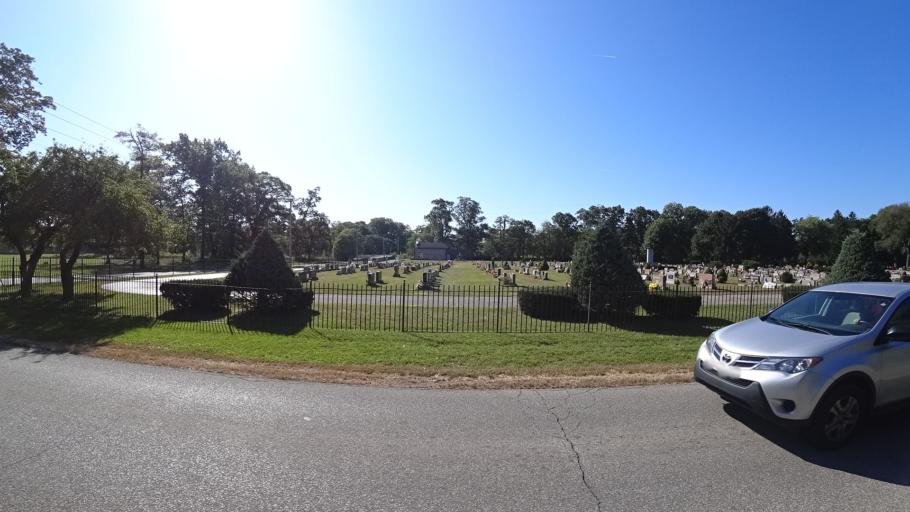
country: US
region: Indiana
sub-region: LaPorte County
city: Michigan City
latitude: 41.7022
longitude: -86.8796
